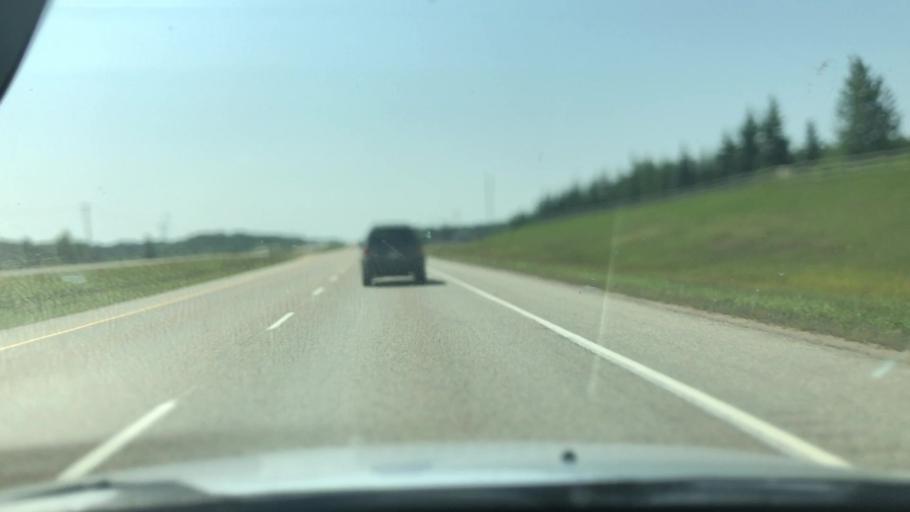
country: CA
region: Alberta
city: Devon
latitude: 53.4482
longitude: -113.7627
